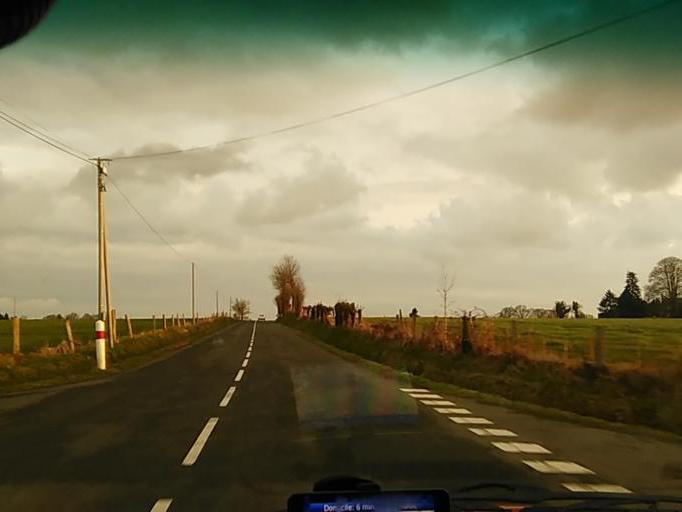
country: FR
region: Lower Normandy
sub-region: Departement de l'Orne
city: La Ferte-Mace
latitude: 48.6204
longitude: -0.3594
